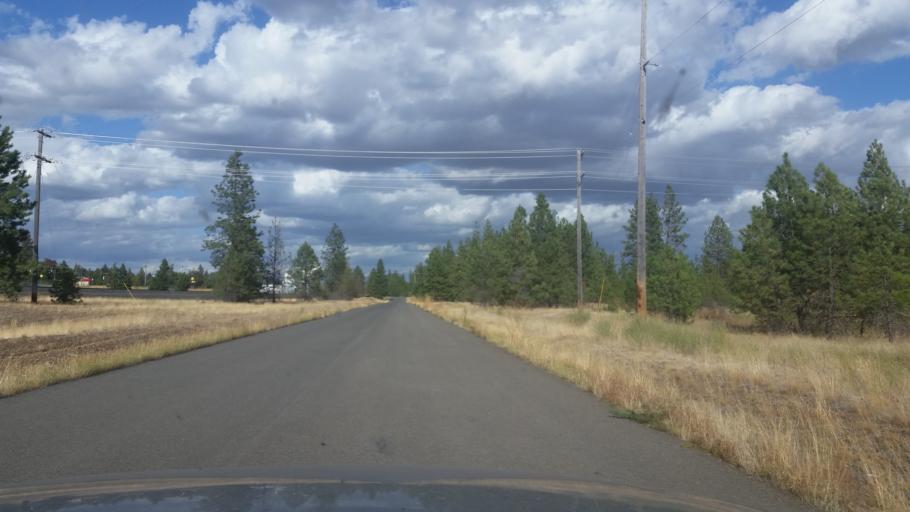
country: US
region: Washington
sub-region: Spokane County
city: Cheney
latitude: 47.4794
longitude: -117.5850
